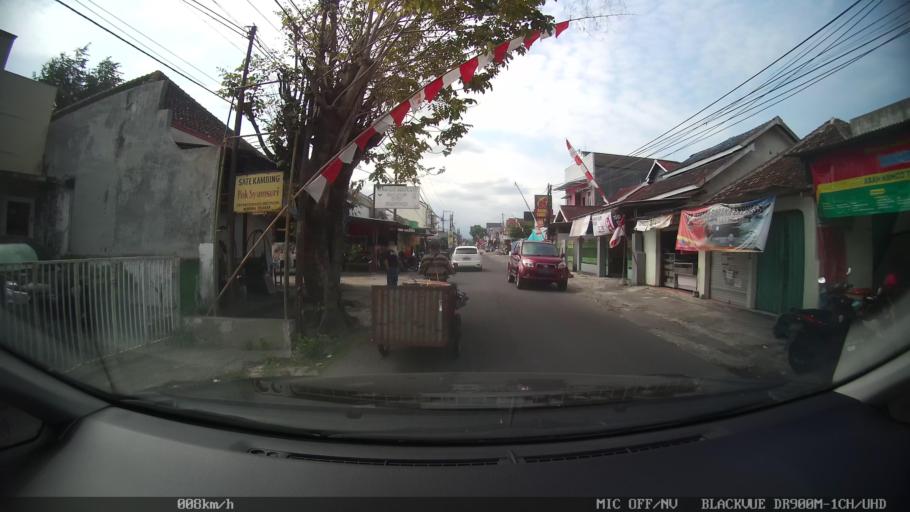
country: ID
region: Daerah Istimewa Yogyakarta
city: Depok
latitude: -7.7786
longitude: 110.4350
